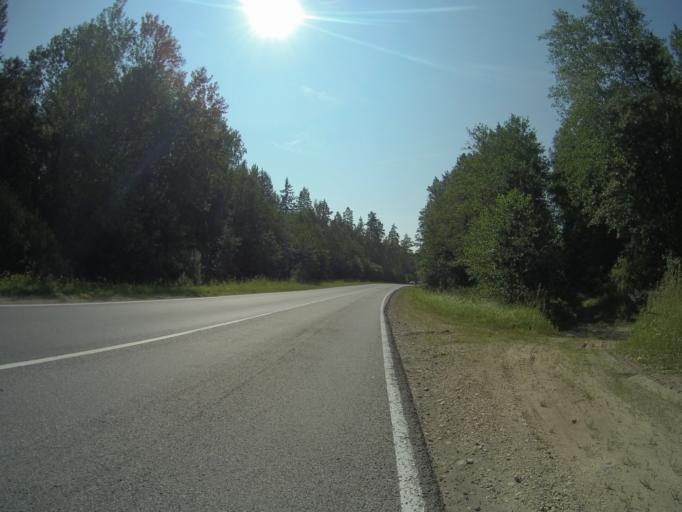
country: RU
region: Vladimir
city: Anopino
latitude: 55.8749
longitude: 40.6291
